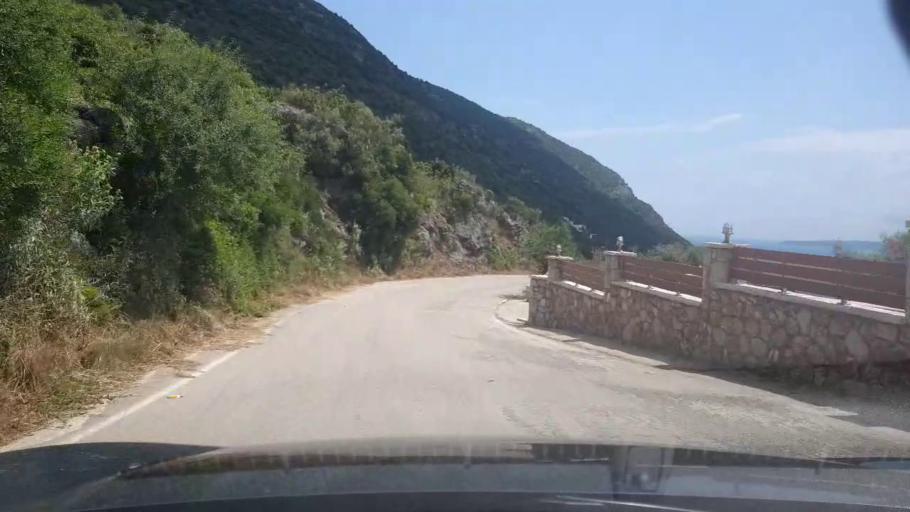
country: GR
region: Ionian Islands
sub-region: Lefkada
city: Nidri
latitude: 38.6440
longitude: 20.6994
